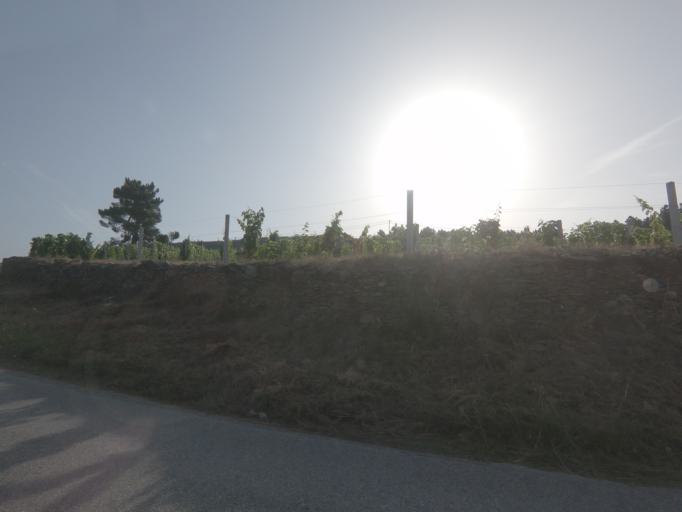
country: PT
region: Vila Real
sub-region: Sabrosa
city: Sabrosa
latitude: 41.2469
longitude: -7.4671
